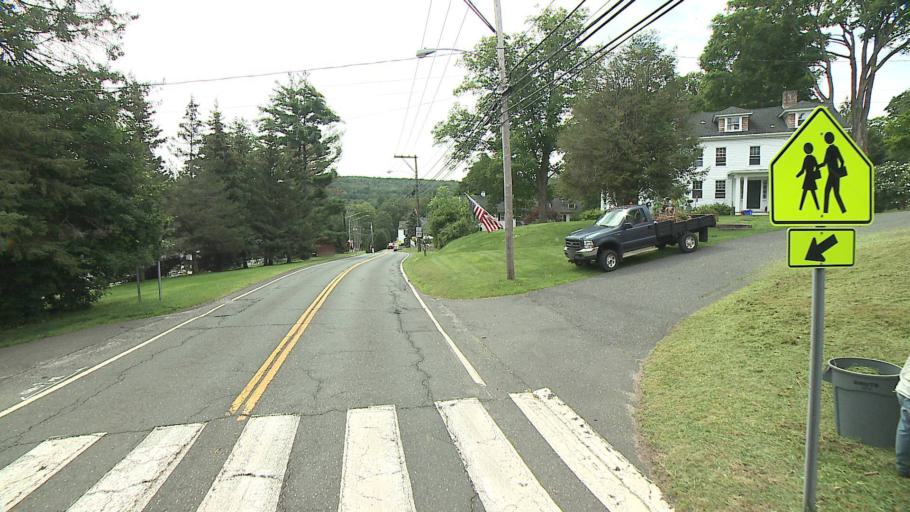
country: US
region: Connecticut
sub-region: Litchfield County
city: New Preston
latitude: 41.6300
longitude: -73.3110
